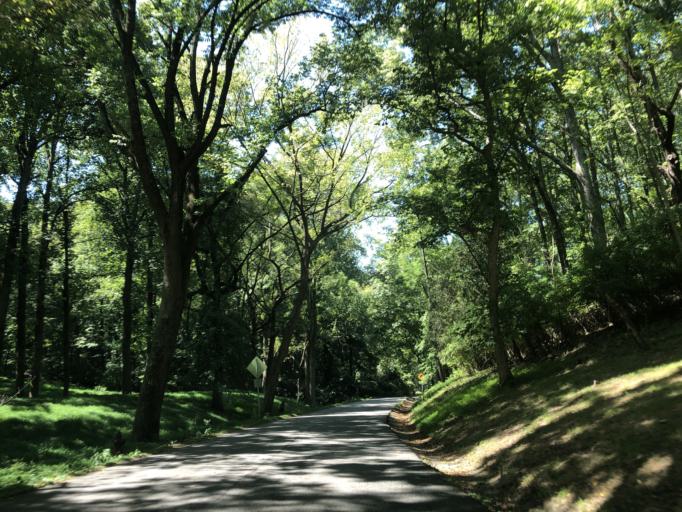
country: US
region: Tennessee
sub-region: Davidson County
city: Oak Hill
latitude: 36.0743
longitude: -86.7870
